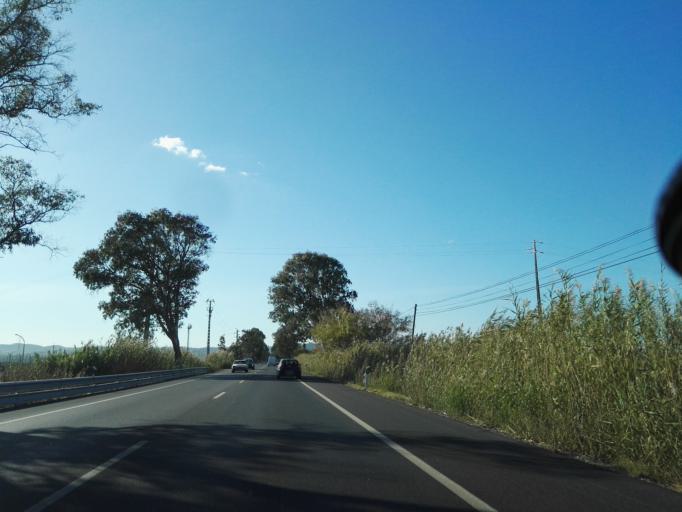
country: PT
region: Santarem
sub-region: Benavente
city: Samora Correia
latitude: 38.9361
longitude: -8.9263
